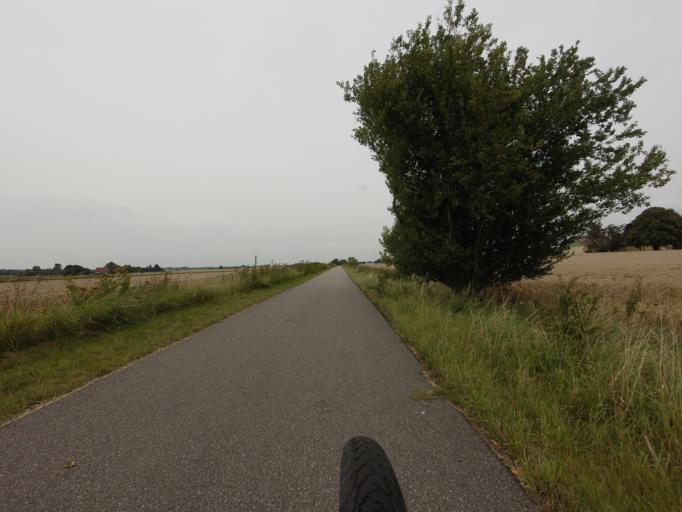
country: DK
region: Zealand
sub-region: Naestved Kommune
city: Fuglebjerg
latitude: 55.2726
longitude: 11.4623
